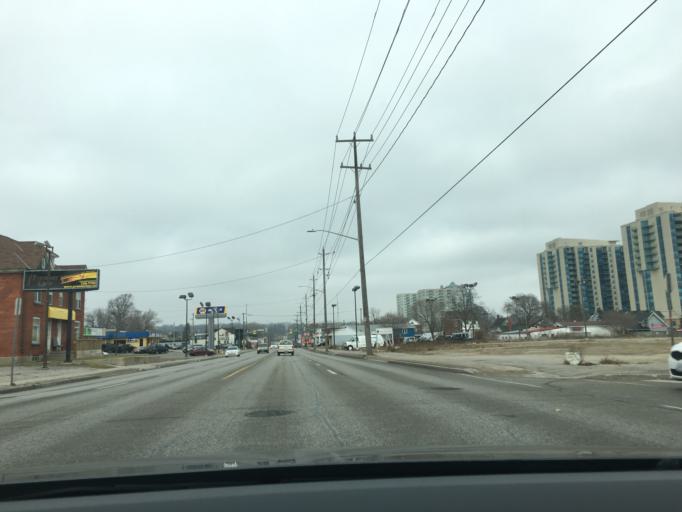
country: CA
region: Ontario
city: Barrie
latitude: 44.3796
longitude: -79.6936
